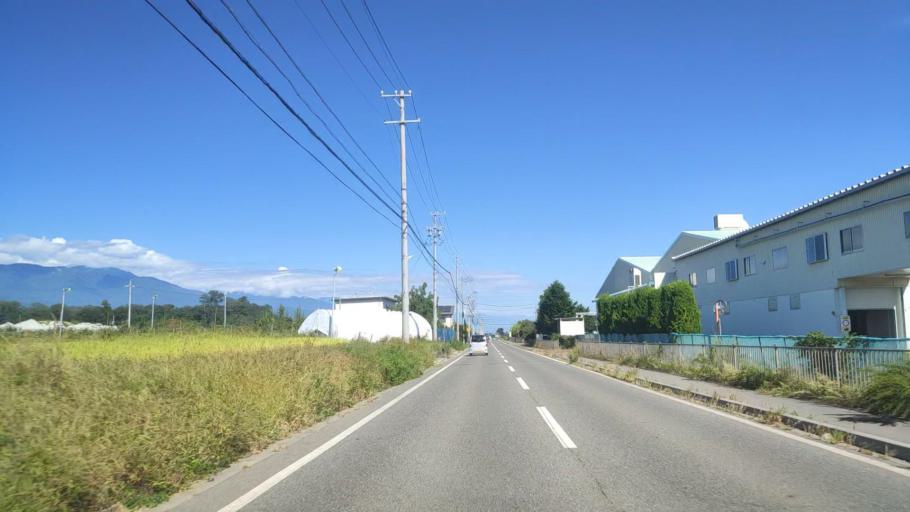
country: JP
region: Nagano
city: Matsumoto
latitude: 36.1734
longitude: 137.9144
